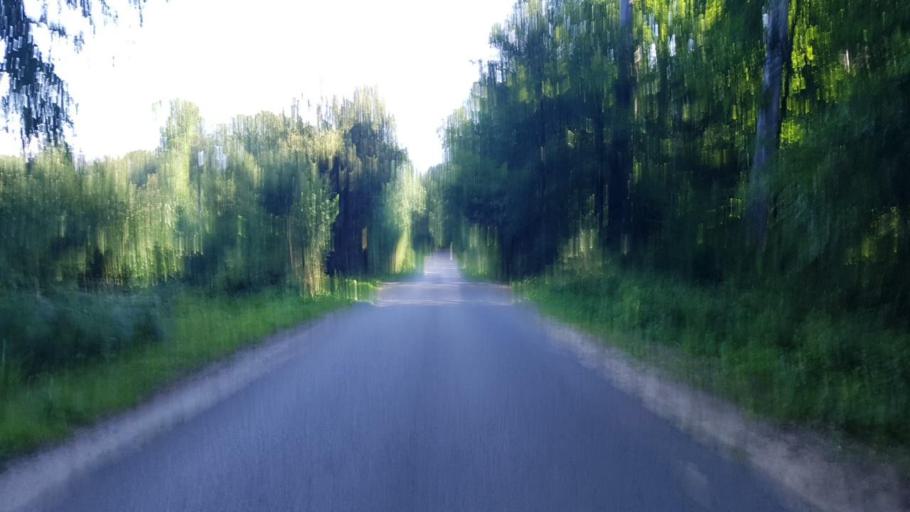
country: FR
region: Picardie
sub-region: Departement de l'Oise
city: Pont-Sainte-Maxence
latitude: 49.2830
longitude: 2.6234
